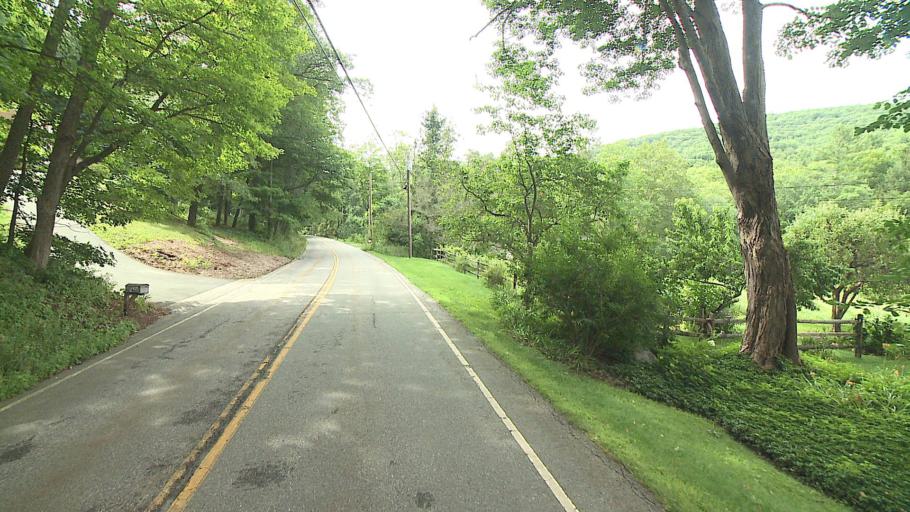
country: US
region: Connecticut
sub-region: Litchfield County
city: Kent
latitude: 41.7493
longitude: -73.5078
